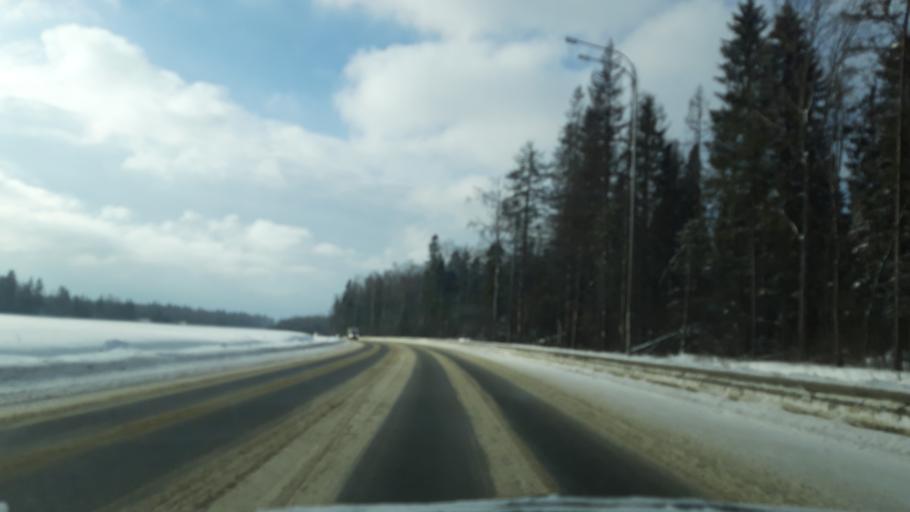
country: RU
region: Moskovskaya
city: Mendeleyevo
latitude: 56.1232
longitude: 37.2993
